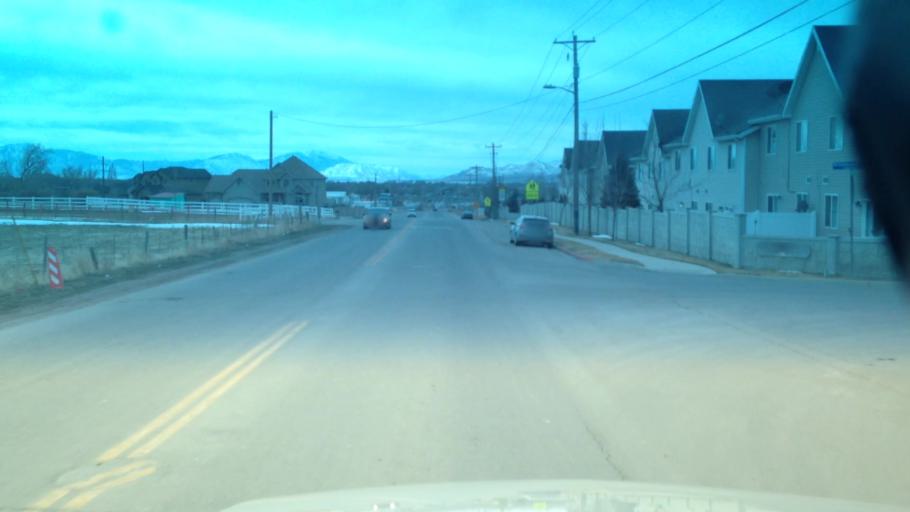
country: US
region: Utah
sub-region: Utah County
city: Lehi
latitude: 40.4243
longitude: -111.8688
